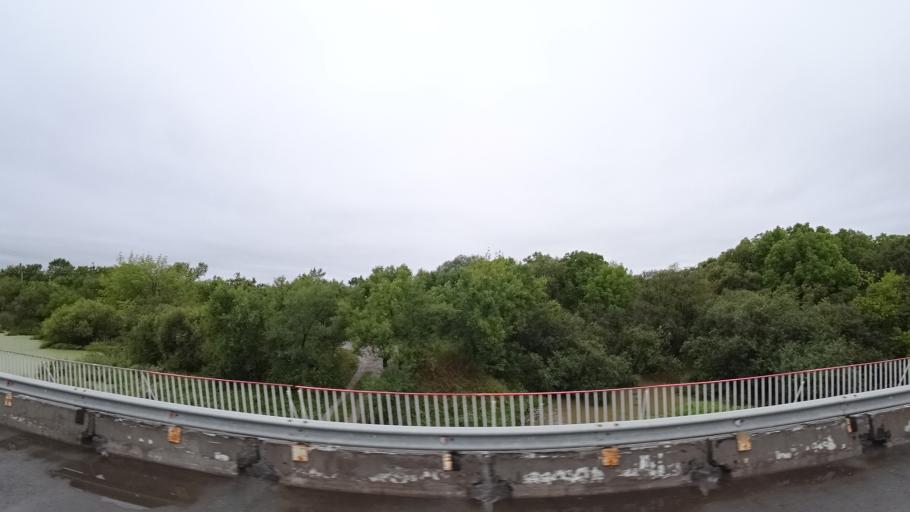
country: RU
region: Primorskiy
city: Monastyrishche
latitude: 44.2171
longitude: 132.4508
